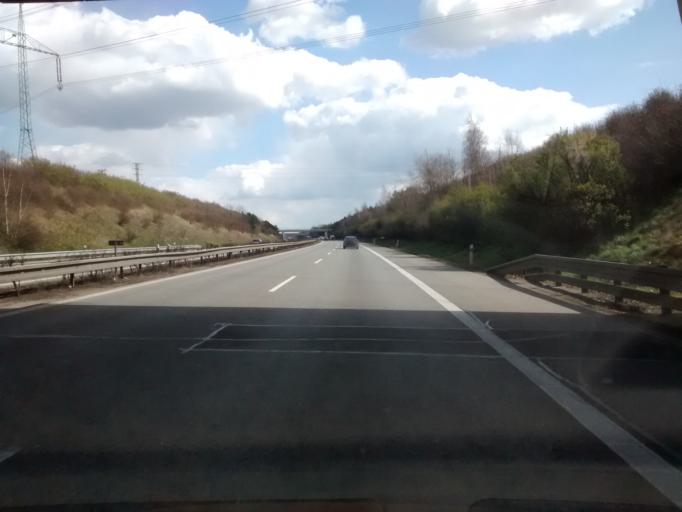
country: CZ
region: Central Bohemia
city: Odolena Voda
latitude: 50.2269
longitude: 14.4039
